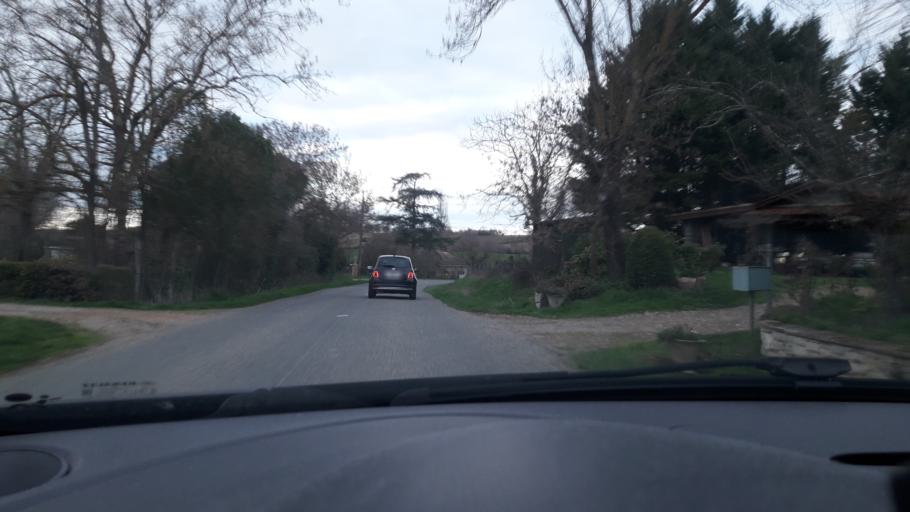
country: FR
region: Midi-Pyrenees
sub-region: Departement du Gers
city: Pujaudran
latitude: 43.6908
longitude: 1.0398
